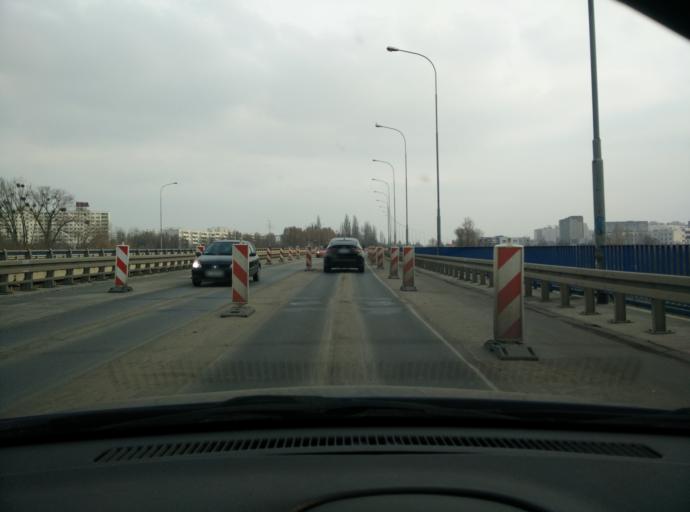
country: PL
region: Greater Poland Voivodeship
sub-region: Poznan
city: Poznan
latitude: 52.3912
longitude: 16.9631
